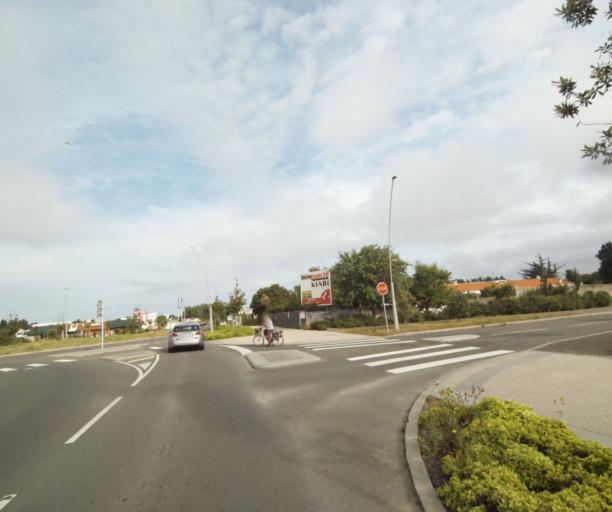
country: FR
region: Pays de la Loire
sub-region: Departement de la Vendee
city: Chateau-d'Olonne
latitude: 46.4881
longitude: -1.7459
